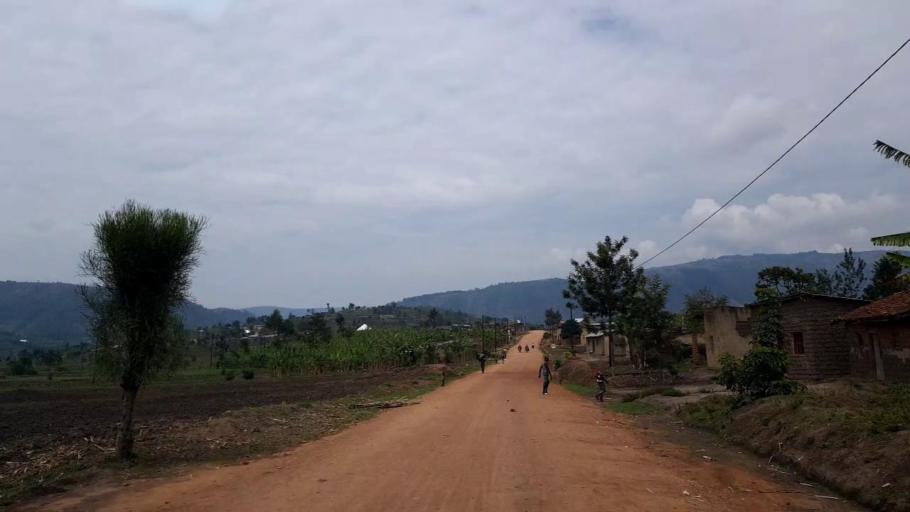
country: RW
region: Northern Province
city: Byumba
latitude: -1.4990
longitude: 30.2183
